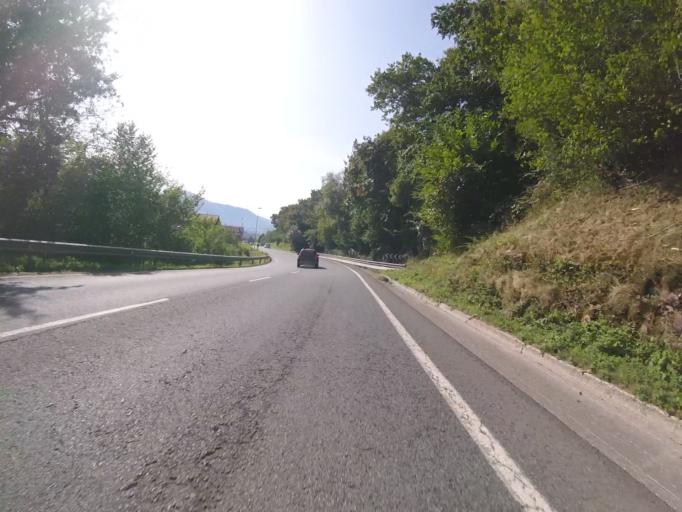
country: ES
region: Navarre
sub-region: Provincia de Navarra
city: Zugarramurdi
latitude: 43.2100
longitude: -1.4897
